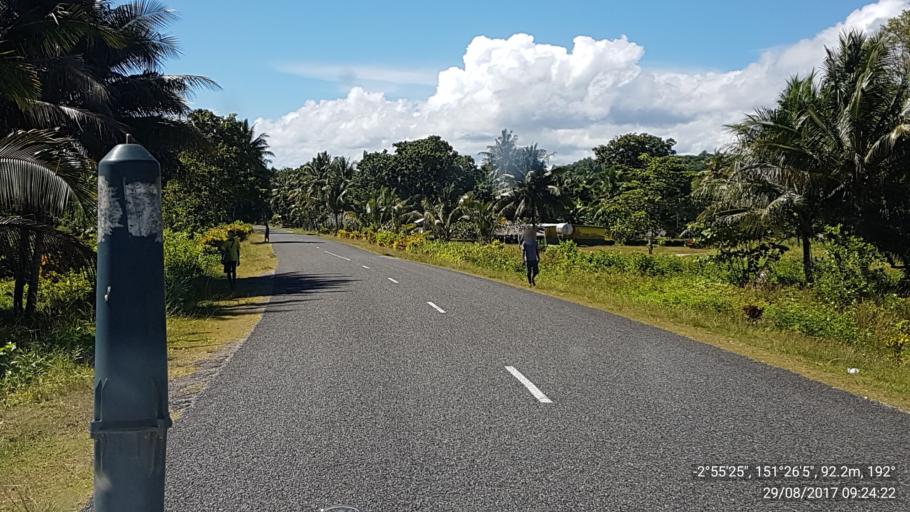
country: PG
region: New Ireland
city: Kavieng
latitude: -2.9236
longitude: 151.4347
